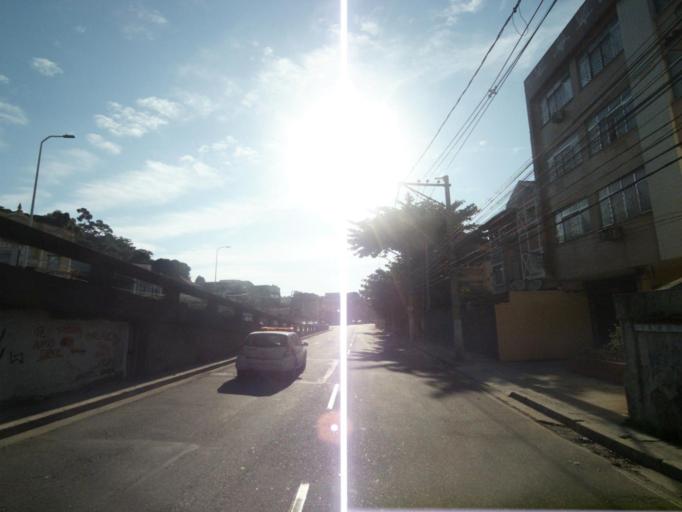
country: BR
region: Rio de Janeiro
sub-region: Niteroi
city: Niteroi
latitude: -22.8808
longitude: -43.1081
